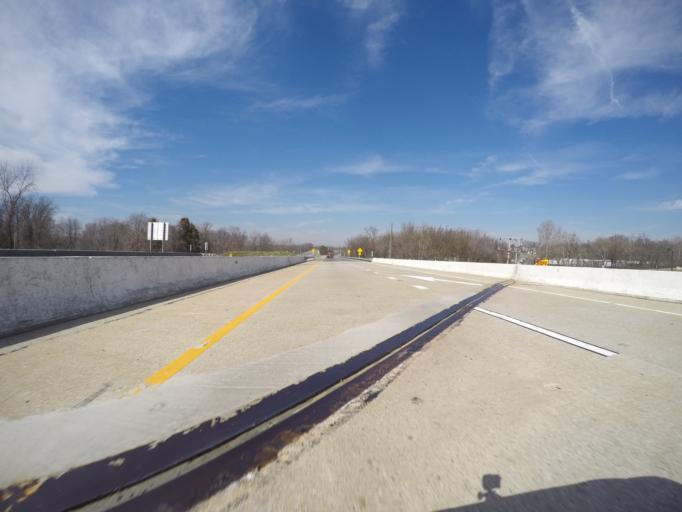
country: US
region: Maryland
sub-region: Anne Arundel County
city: Brooklyn Park
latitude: 39.2217
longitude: -76.6247
